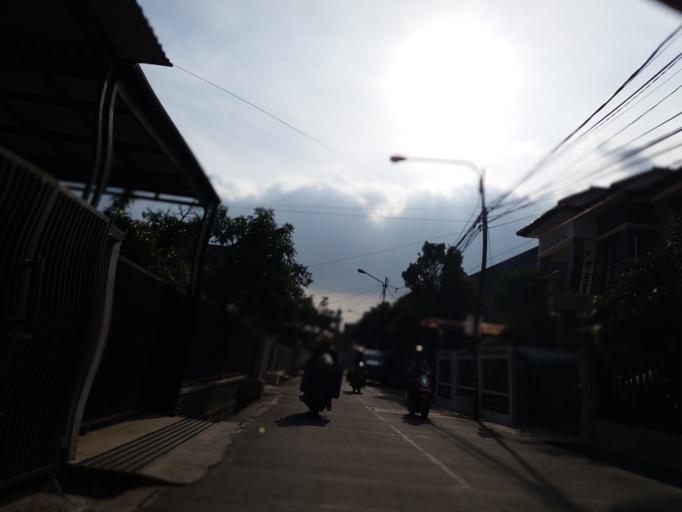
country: ID
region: West Java
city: Bandung
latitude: -6.9536
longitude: 107.6346
